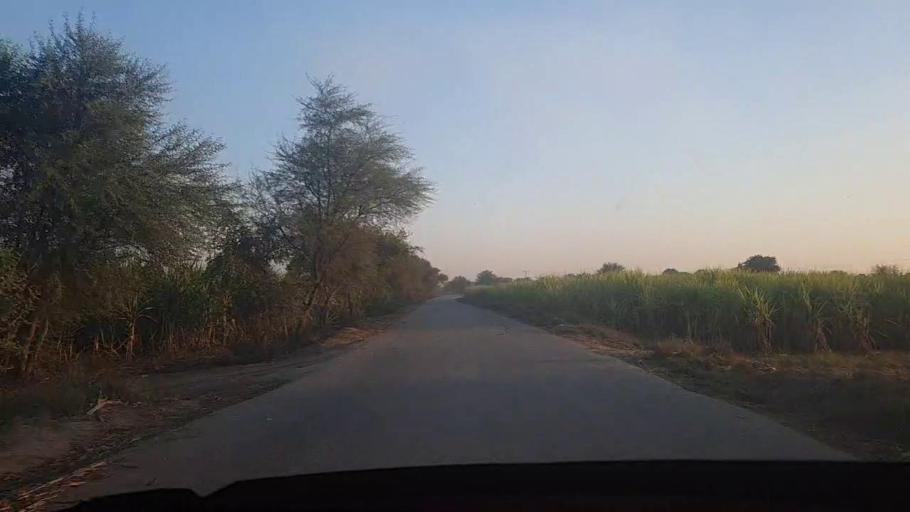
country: PK
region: Sindh
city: Sobhadero
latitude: 27.3425
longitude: 68.3781
